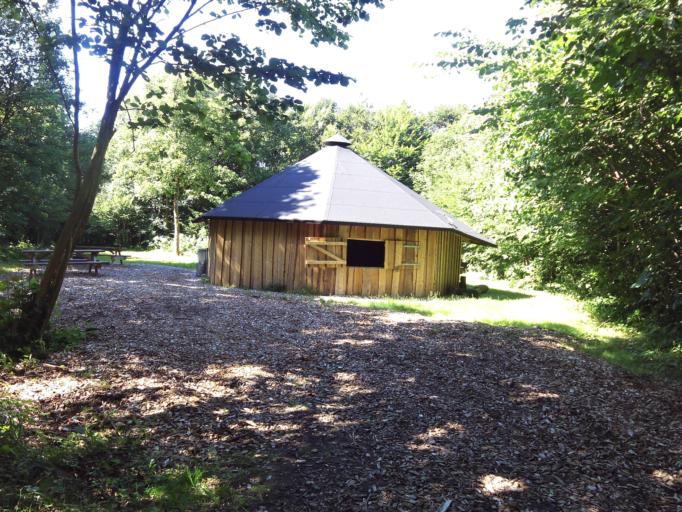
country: DK
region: South Denmark
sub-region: Vejen Kommune
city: Rodding
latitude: 55.3764
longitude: 9.0861
